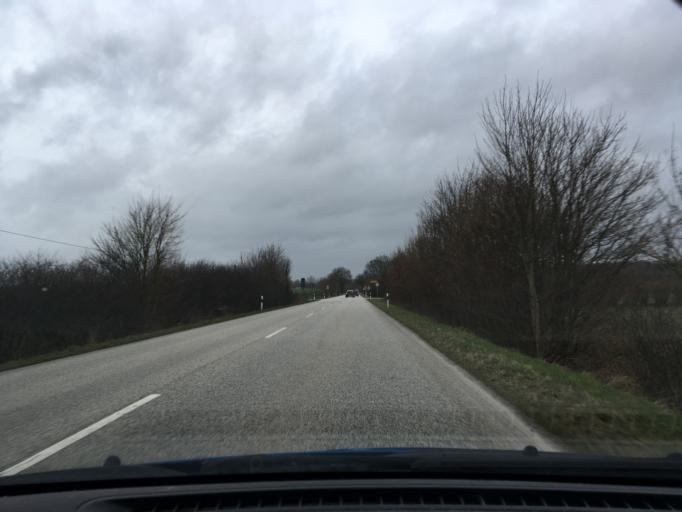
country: DE
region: Schleswig-Holstein
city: Kruzen
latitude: 53.4051
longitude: 10.5387
